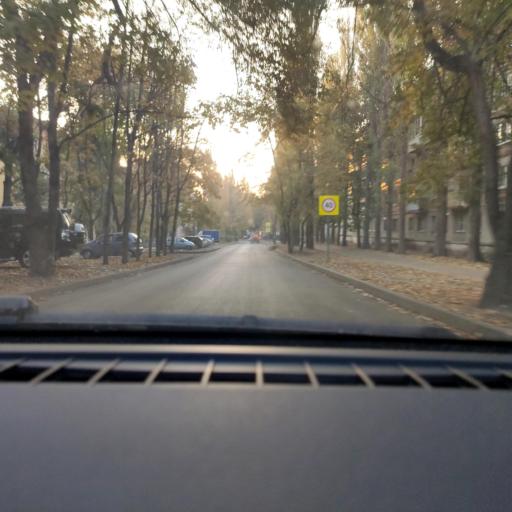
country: RU
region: Voronezj
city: Maslovka
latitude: 51.6144
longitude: 39.2498
